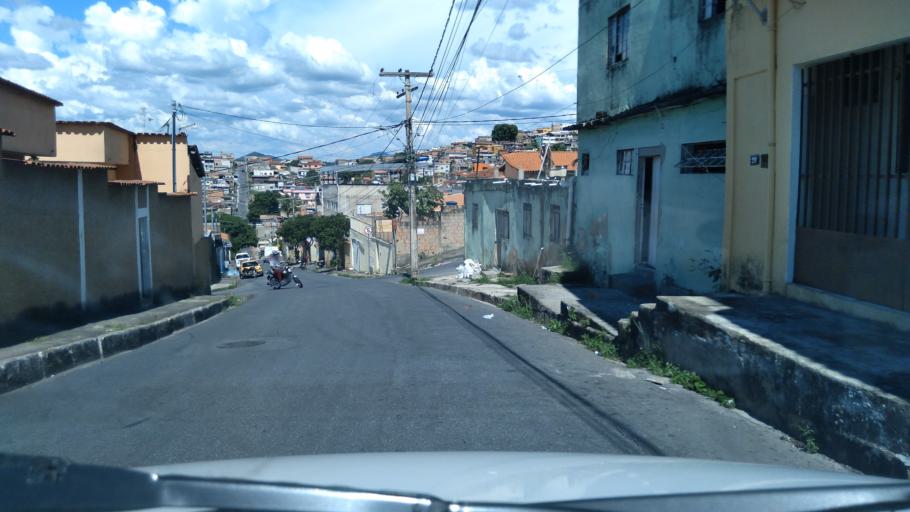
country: BR
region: Minas Gerais
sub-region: Belo Horizonte
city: Belo Horizonte
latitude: -19.8719
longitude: -43.9128
